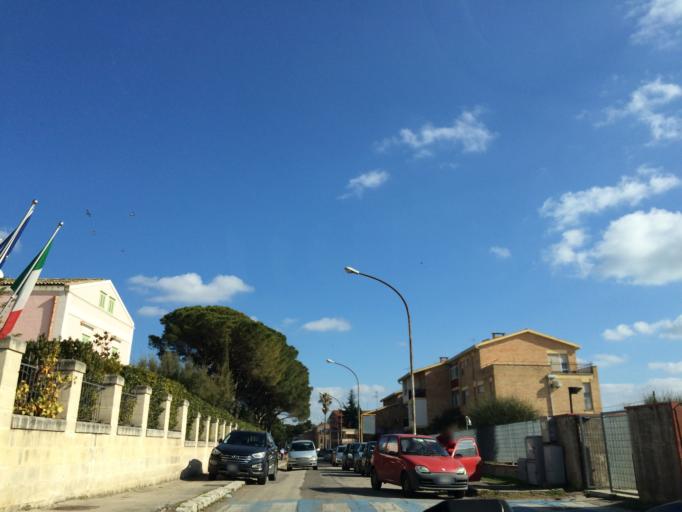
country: IT
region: Basilicate
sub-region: Provincia di Matera
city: Matera
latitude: 40.6582
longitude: 16.6108
